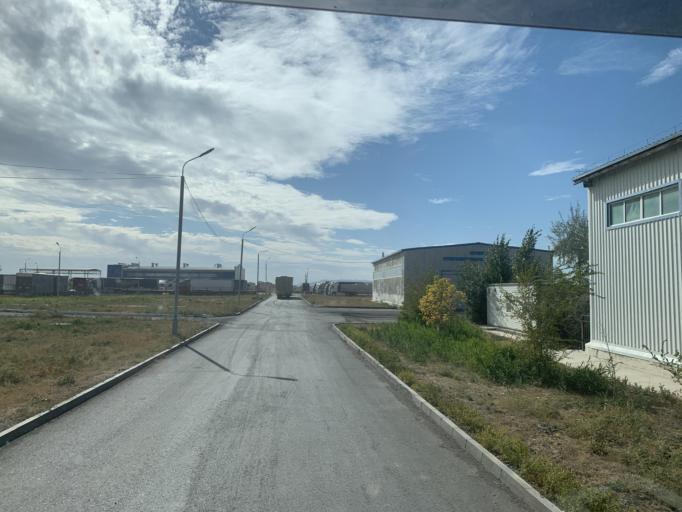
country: CN
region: Xinjiang Uygur Zizhiqu
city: Tacheng
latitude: 46.6799
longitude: 82.7759
